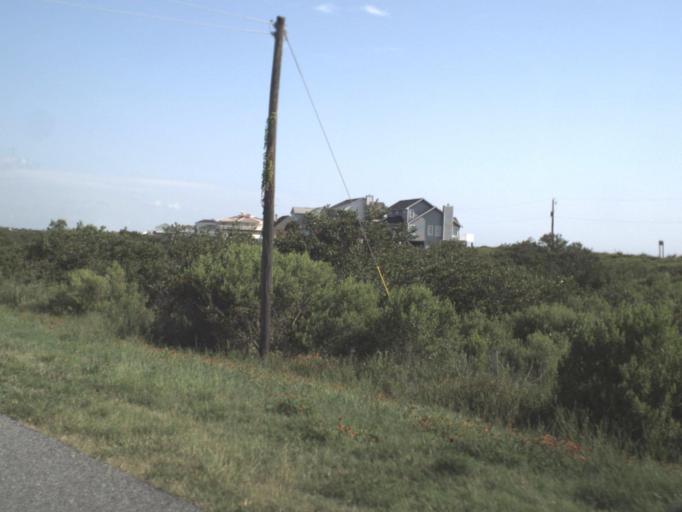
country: US
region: Florida
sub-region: Flagler County
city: Palm Coast
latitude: 29.6750
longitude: -81.2162
